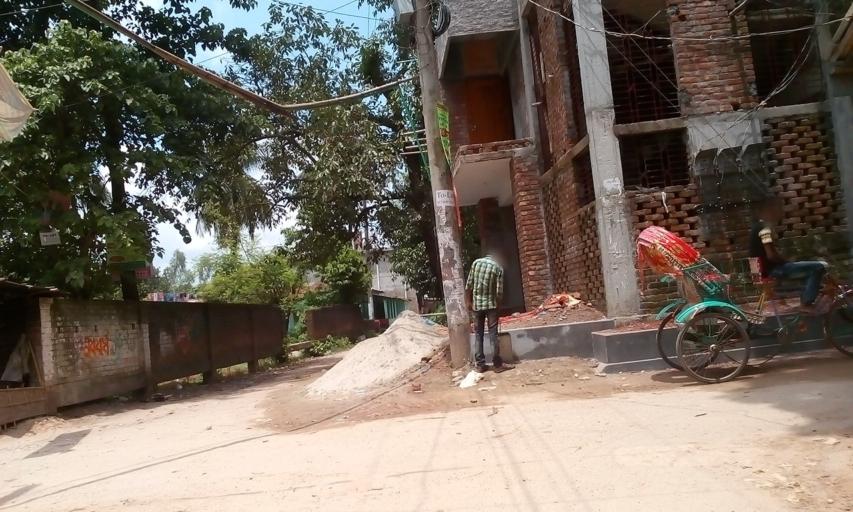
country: IN
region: West Bengal
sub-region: Dakshin Dinajpur
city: Balurghat
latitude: 25.3875
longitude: 88.9940
